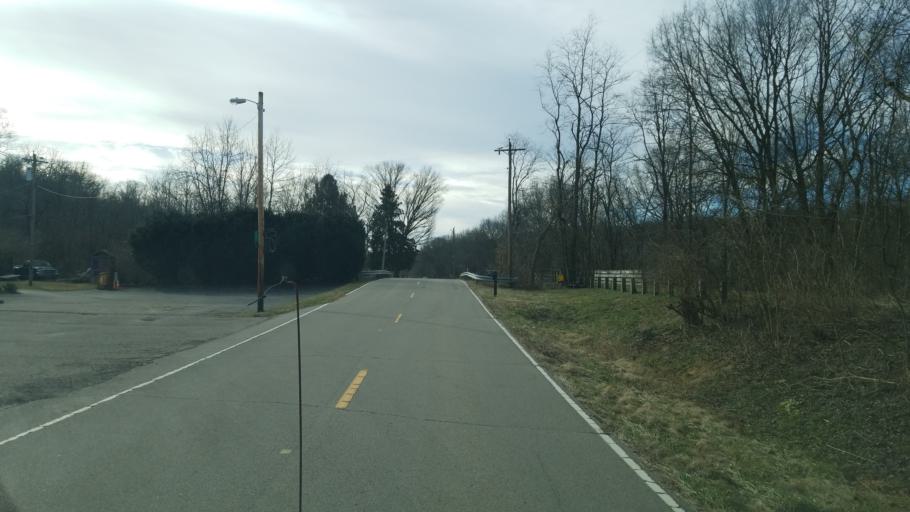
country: US
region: Ohio
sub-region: Warren County
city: Waynesville
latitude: 39.4455
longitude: -84.0991
